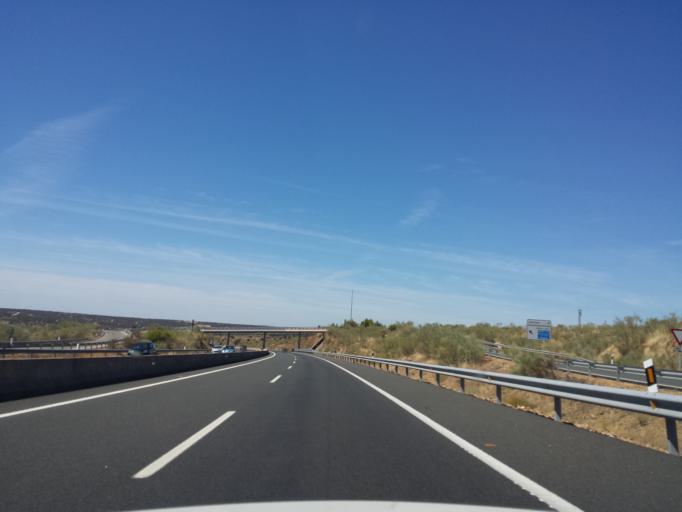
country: ES
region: Extremadura
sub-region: Provincia de Caceres
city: Jaraicejo
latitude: 39.6607
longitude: -5.7927
